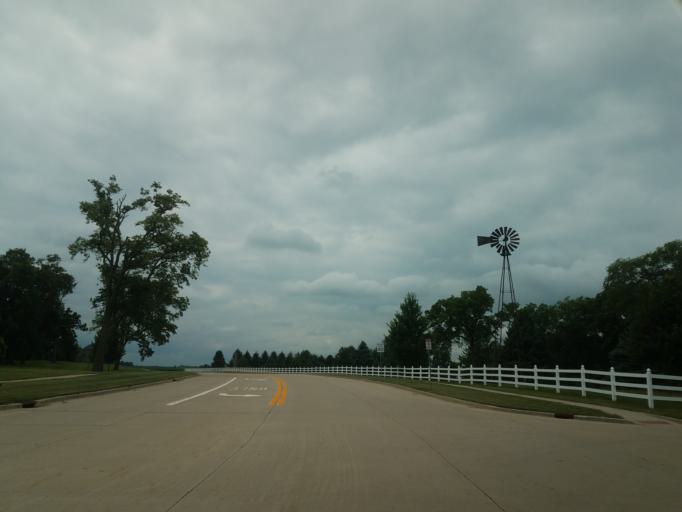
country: US
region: Illinois
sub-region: McLean County
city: Twin Grove
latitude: 40.4459
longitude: -89.0503
